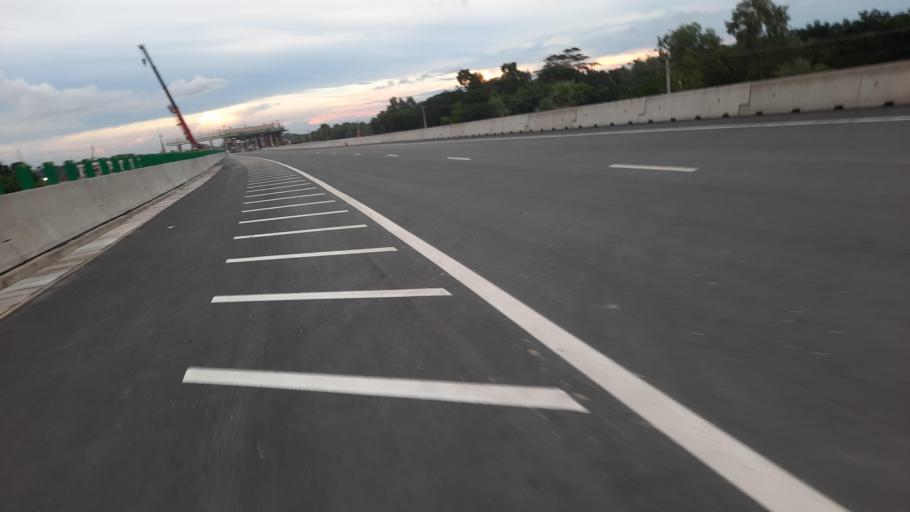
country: BD
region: Khulna
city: Kalia
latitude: 23.1903
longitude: 89.7025
